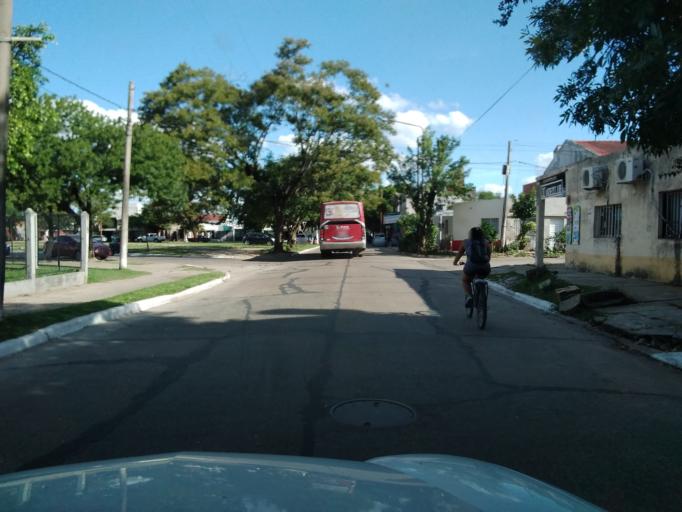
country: AR
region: Corrientes
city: Corrientes
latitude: -27.4896
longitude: -58.8329
